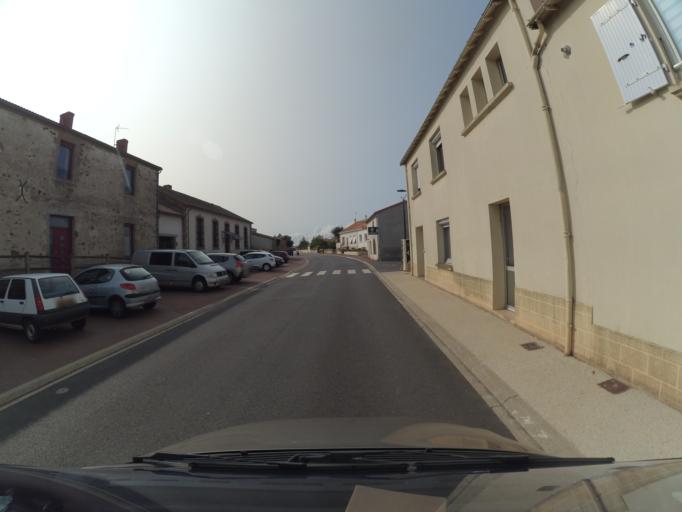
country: FR
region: Pays de la Loire
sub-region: Departement de la Vendee
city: La Guyonniere
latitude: 46.9654
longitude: -1.2502
